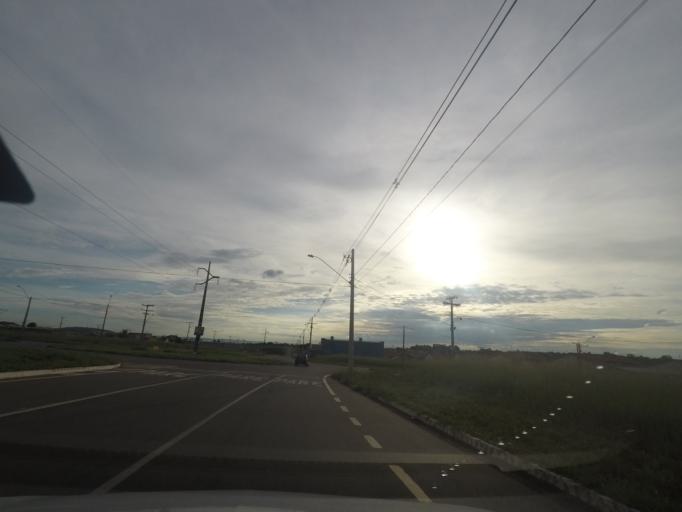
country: BR
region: Goias
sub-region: Trindade
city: Trindade
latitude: -16.7202
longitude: -49.3960
